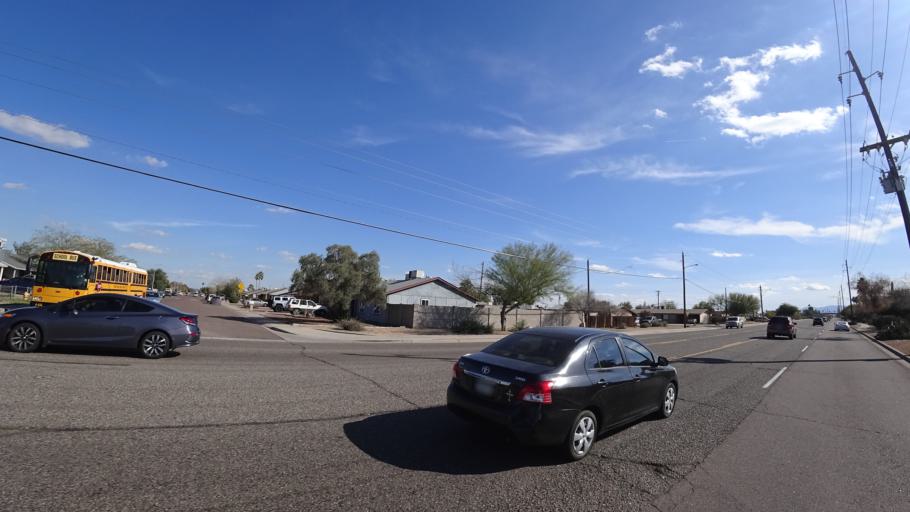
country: US
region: Arizona
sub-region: Maricopa County
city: Peoria
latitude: 33.5779
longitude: -112.2204
